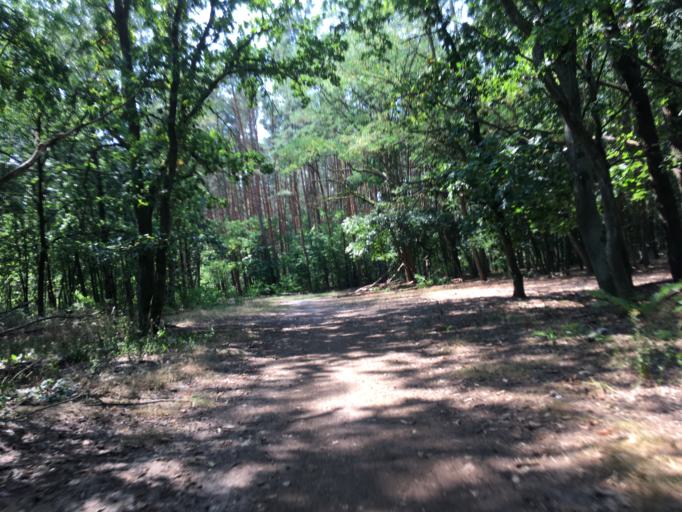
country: DE
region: Berlin
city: Friedrichshagen
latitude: 52.4718
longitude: 13.6073
